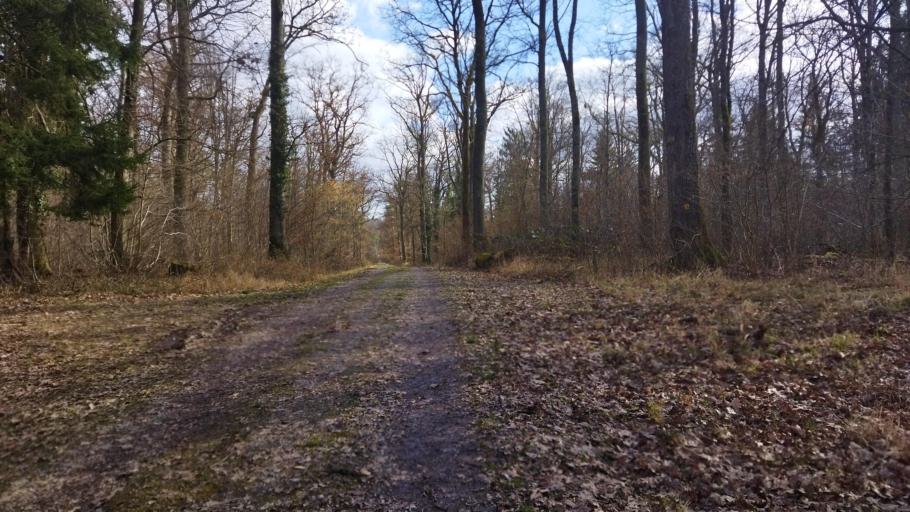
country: DE
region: Baden-Wuerttemberg
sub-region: Regierungsbezirk Stuttgart
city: Freudental
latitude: 48.9989
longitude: 9.0612
